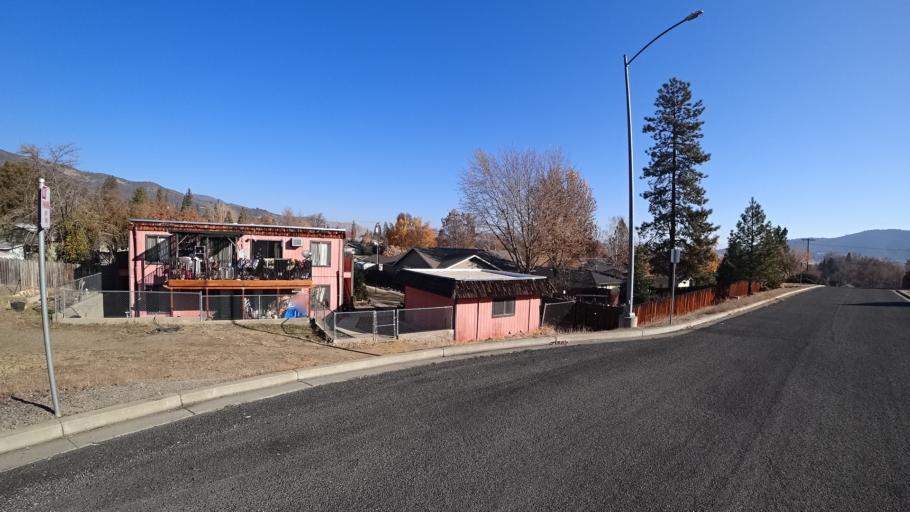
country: US
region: California
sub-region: Siskiyou County
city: Yreka
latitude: 41.7334
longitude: -122.6473
